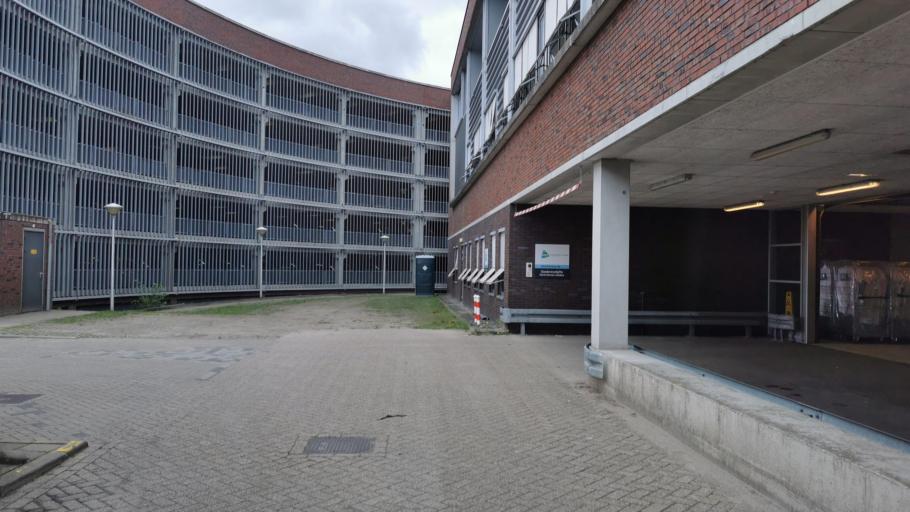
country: NL
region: Overijssel
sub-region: Gemeente Enschede
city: Enschede
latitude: 52.2153
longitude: 6.8915
